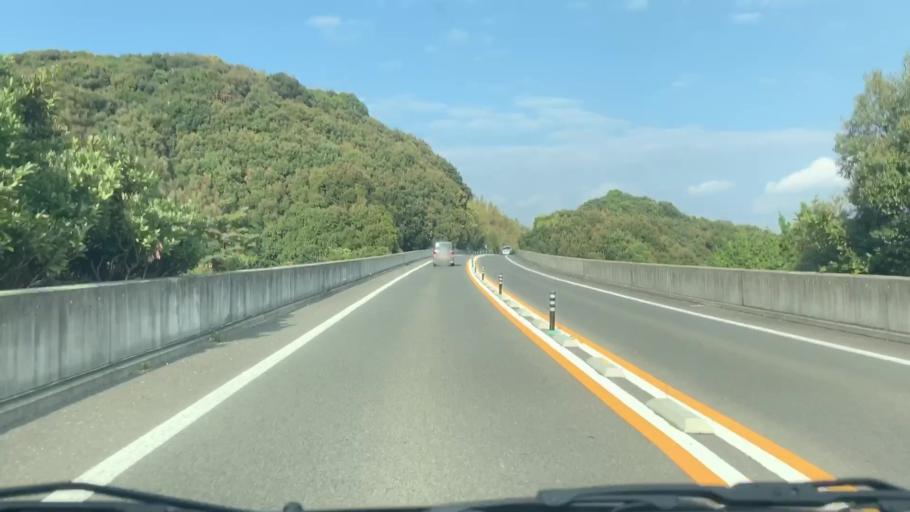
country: JP
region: Nagasaki
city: Sasebo
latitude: 33.0302
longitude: 129.7388
